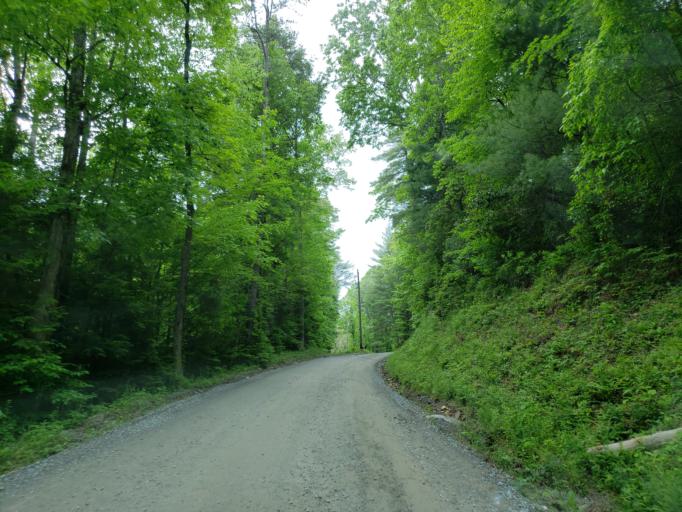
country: US
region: Georgia
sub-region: Fannin County
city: Blue Ridge
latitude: 34.8580
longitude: -84.4234
